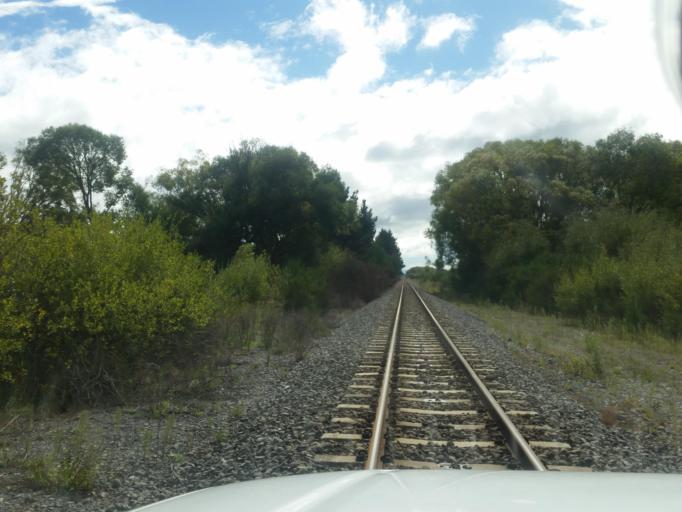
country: NZ
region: Canterbury
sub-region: Waimakariri District
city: Kaiapoi
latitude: -43.4047
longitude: 172.6502
